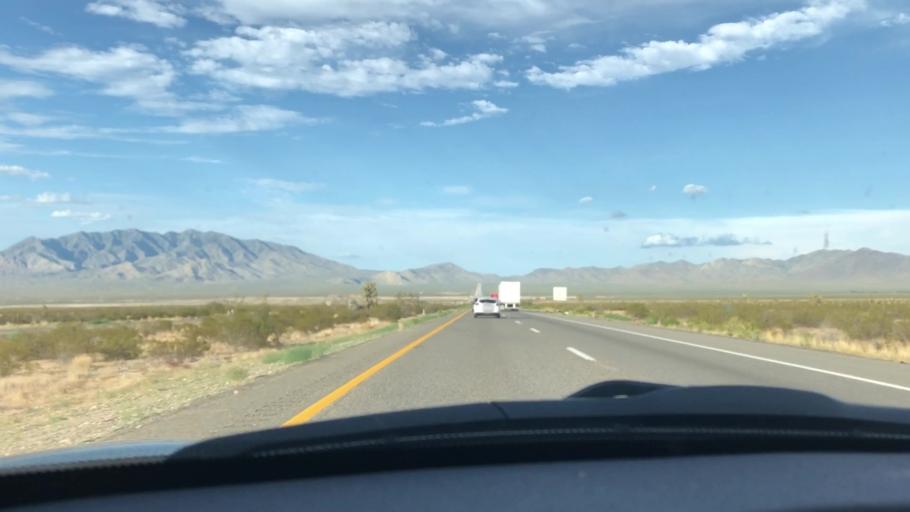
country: US
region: Nevada
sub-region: Clark County
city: Sandy Valley
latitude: 35.4266
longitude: -115.7233
